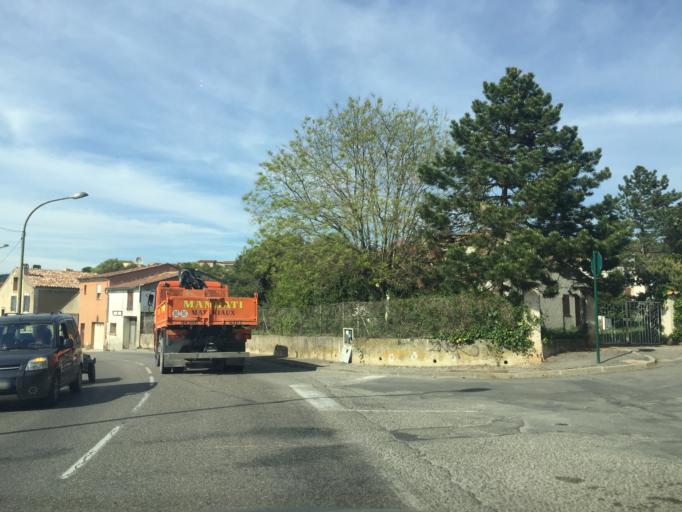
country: FR
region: Provence-Alpes-Cote d'Azur
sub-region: Departement du Var
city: Vinon-sur-Verdon
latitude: 43.7212
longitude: 5.8129
